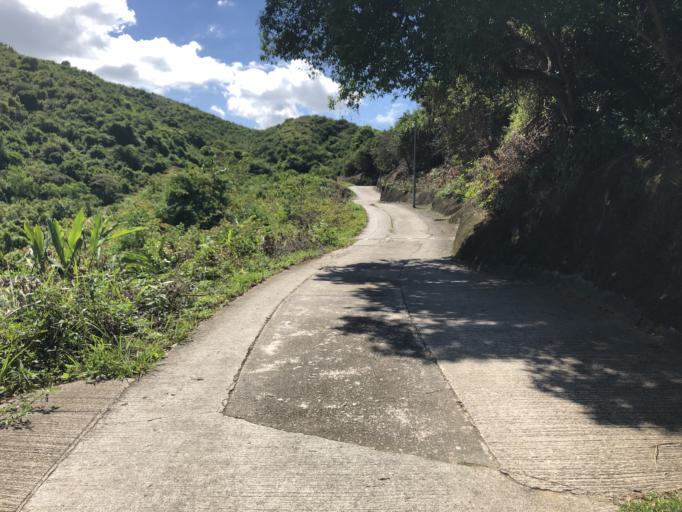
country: HK
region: Tuen Mun
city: Tuen Mun
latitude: 22.2923
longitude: 113.9765
